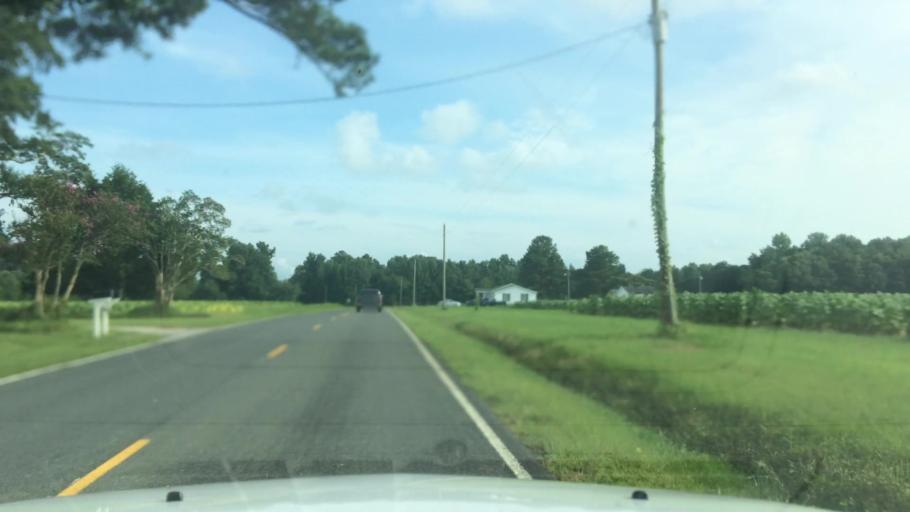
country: US
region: North Carolina
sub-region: Greene County
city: Maury
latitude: 35.4895
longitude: -77.5201
